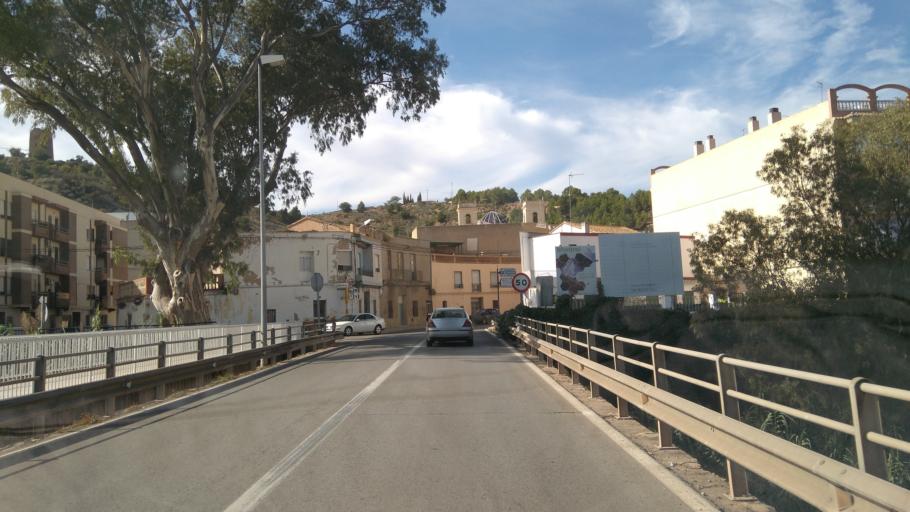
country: ES
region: Valencia
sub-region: Provincia de Valencia
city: Montroy
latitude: 39.3373
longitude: -0.6125
